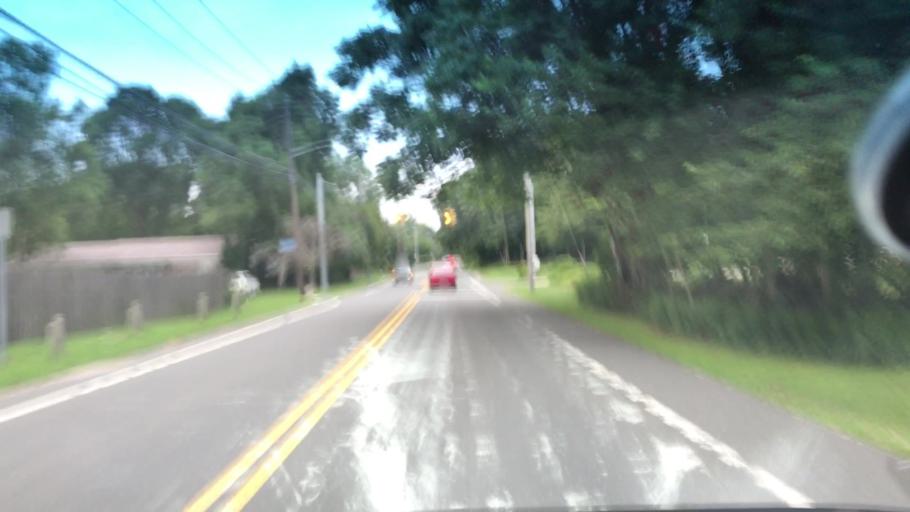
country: US
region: New York
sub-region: Suffolk County
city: Wading River
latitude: 40.9584
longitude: -72.8083
